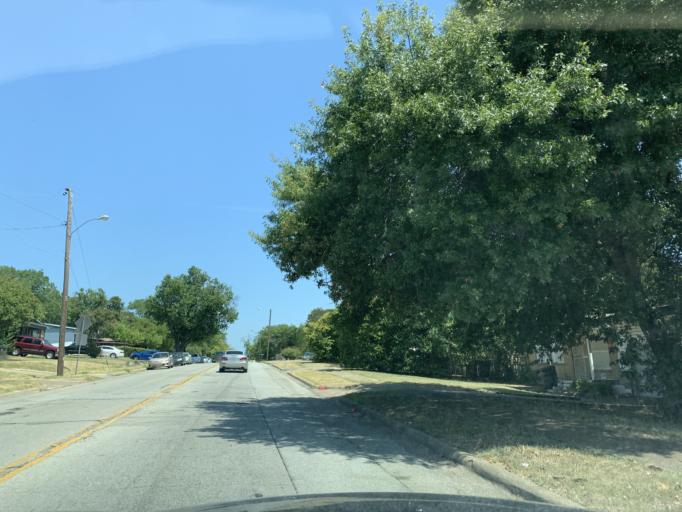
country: US
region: Texas
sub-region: Dallas County
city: Cockrell Hill
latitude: 32.6923
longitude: -96.8091
